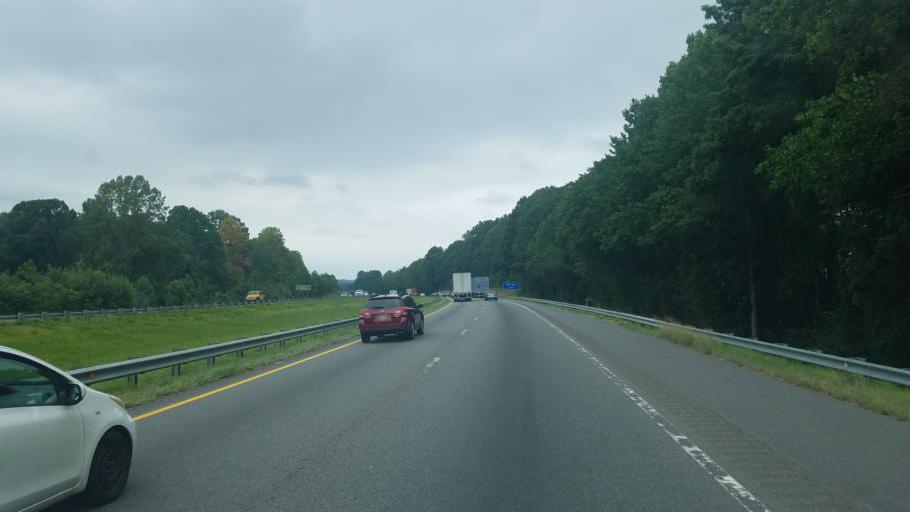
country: US
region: North Carolina
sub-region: Iredell County
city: Mooresville
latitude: 35.6162
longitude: -80.8571
